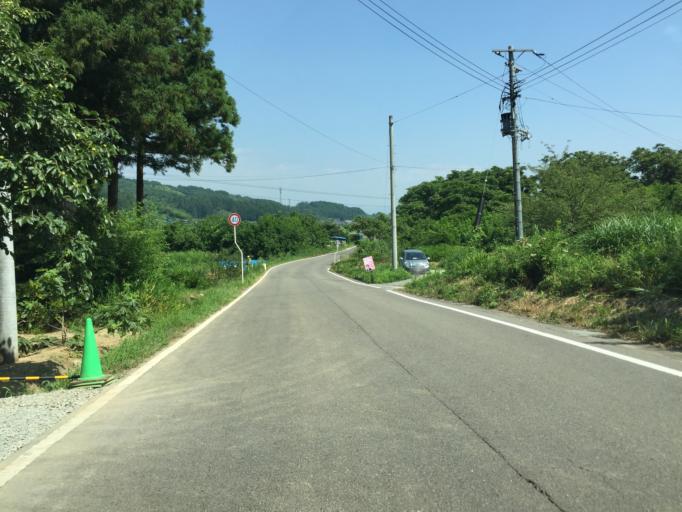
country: JP
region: Fukushima
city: Fukushima-shi
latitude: 37.6965
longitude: 140.4462
